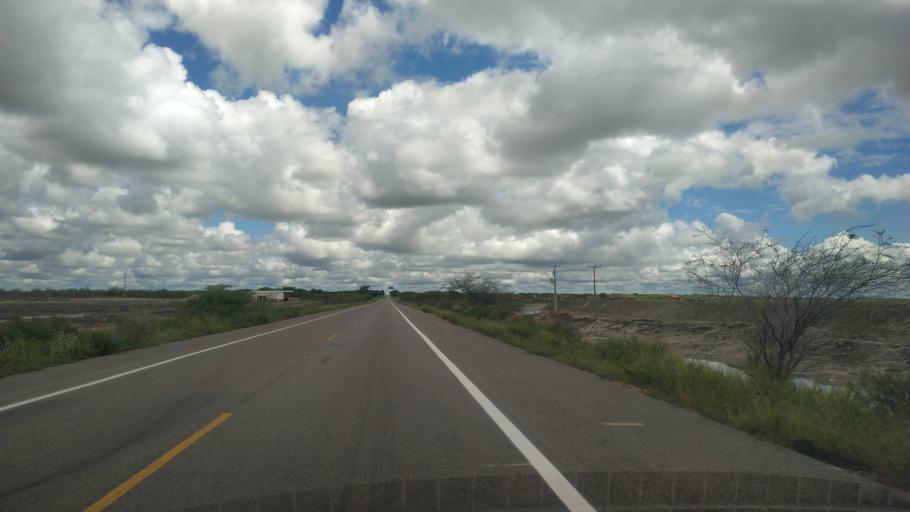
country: BR
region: Rio Grande do Norte
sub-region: Areia Branca
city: Areia Branca
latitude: -5.0520
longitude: -37.1500
